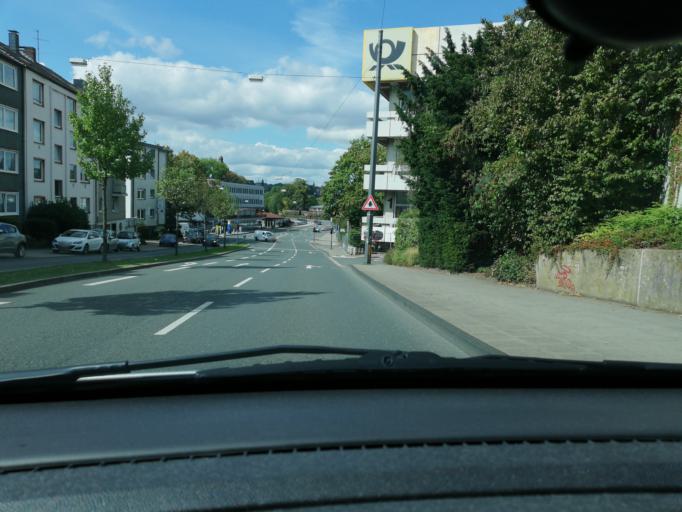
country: DE
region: North Rhine-Westphalia
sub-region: Regierungsbezirk Dusseldorf
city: Wuppertal
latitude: 51.2519
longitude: 7.1474
